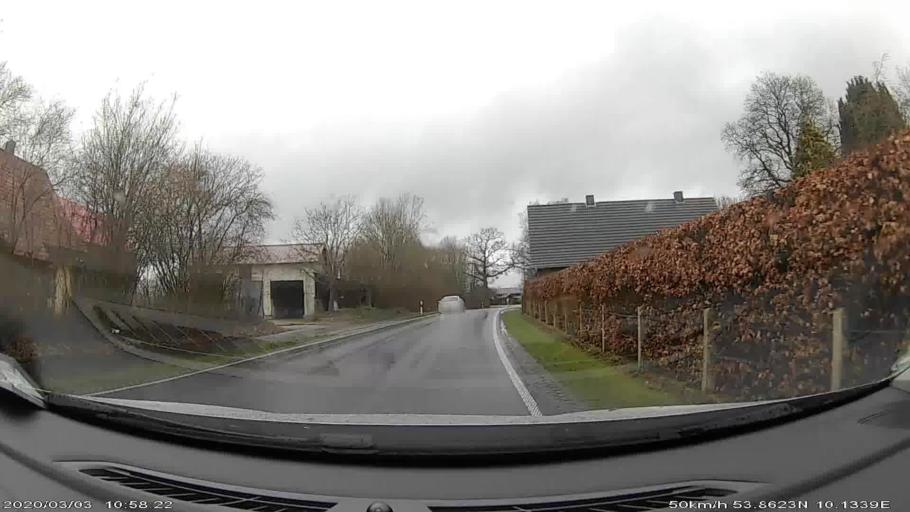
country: DE
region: Schleswig-Holstein
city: Stuvenborn
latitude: 53.8645
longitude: 10.1345
